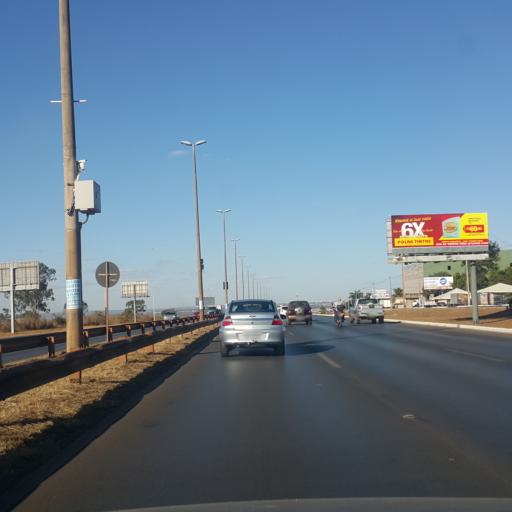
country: BR
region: Federal District
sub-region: Brasilia
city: Brasilia
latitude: -15.7914
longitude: -48.0479
